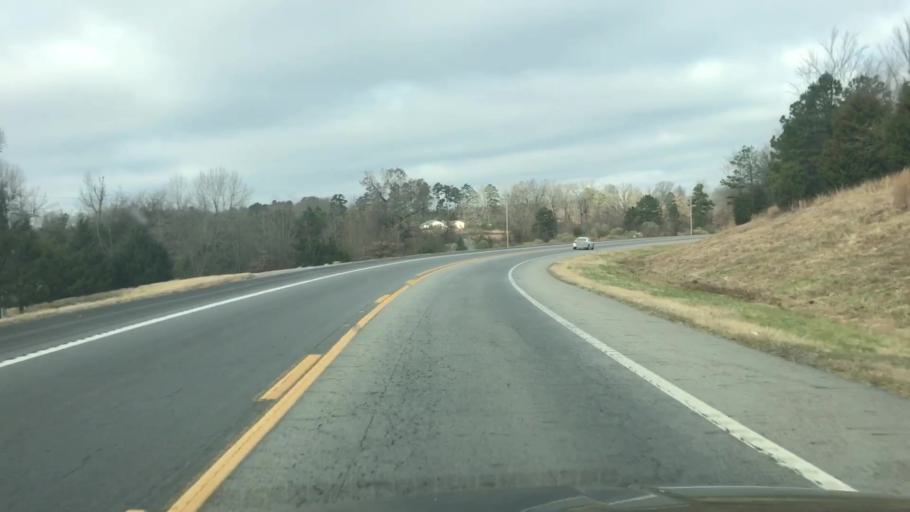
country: US
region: Arkansas
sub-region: Scott County
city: Waldron
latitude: 34.8394
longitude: -94.0517
